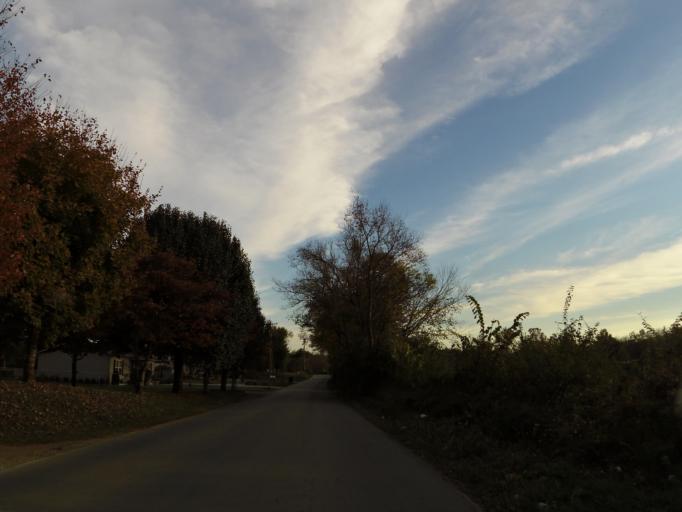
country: US
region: Tennessee
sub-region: Blount County
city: Alcoa
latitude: 35.7854
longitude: -83.9552
